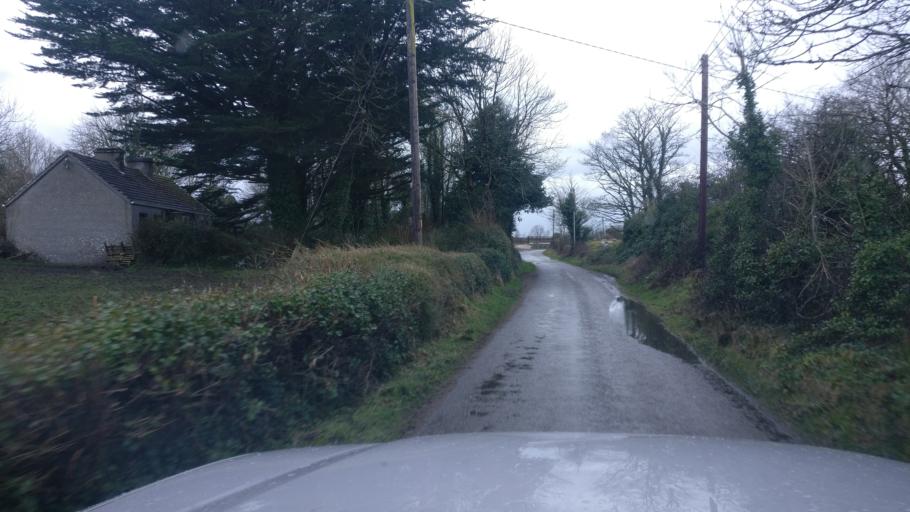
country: IE
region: Connaught
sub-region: County Galway
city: Athenry
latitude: 53.1855
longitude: -8.6988
